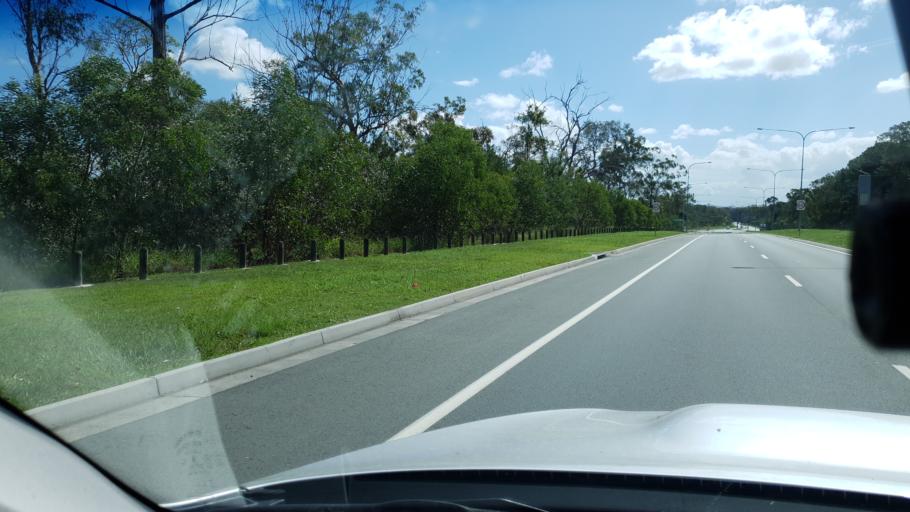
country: AU
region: Queensland
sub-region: Logan
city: Woodridge
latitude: -27.6443
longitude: 153.0977
